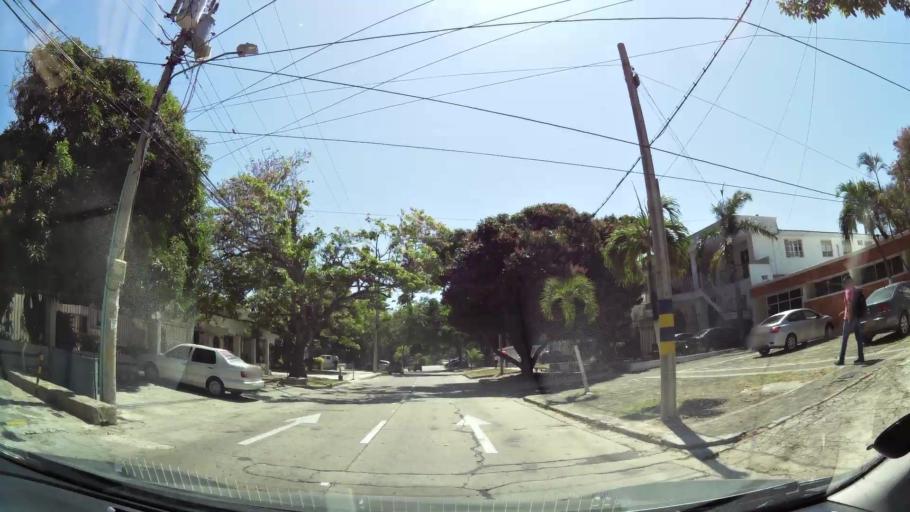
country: CO
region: Atlantico
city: Barranquilla
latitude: 10.9983
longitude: -74.7950
